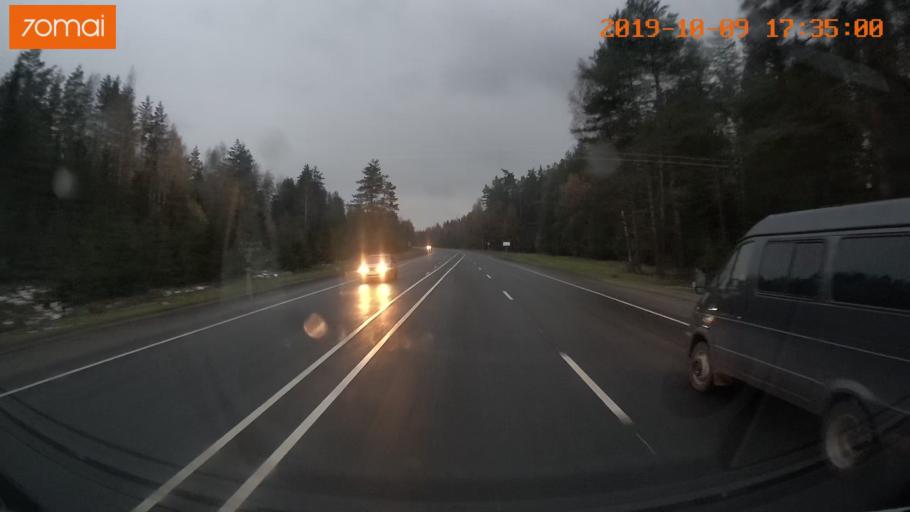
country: RU
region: Ivanovo
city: Bogorodskoye
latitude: 57.1003
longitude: 41.0062
